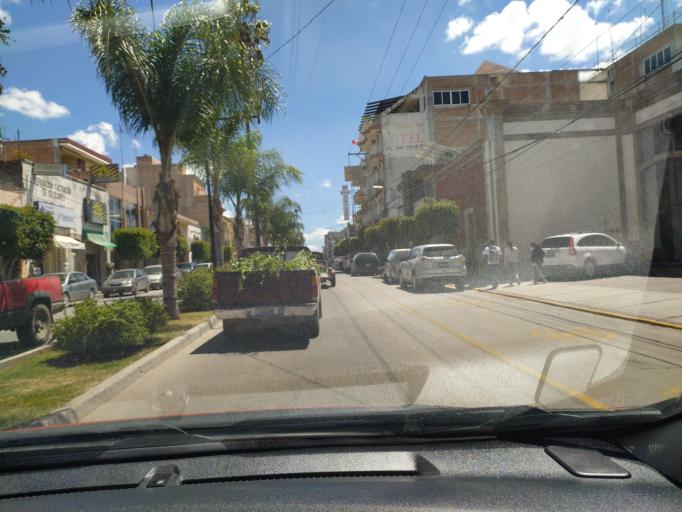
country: MX
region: Jalisco
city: San Julian
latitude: 21.0112
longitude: -102.1824
